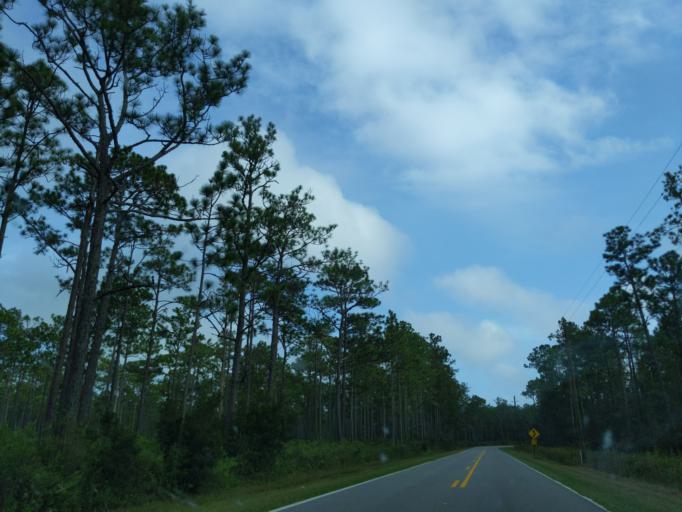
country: US
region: Florida
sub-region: Wakulla County
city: Crawfordville
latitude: 30.1122
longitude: -84.3099
